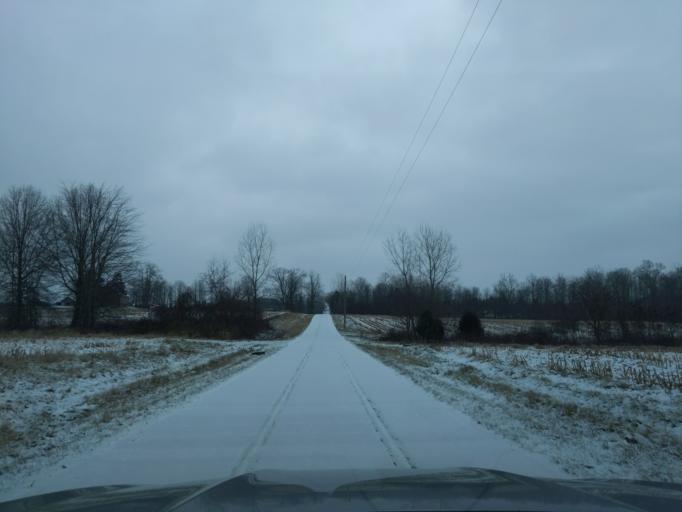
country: US
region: Indiana
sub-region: Decatur County
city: Westport
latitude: 39.2048
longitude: -85.4925
